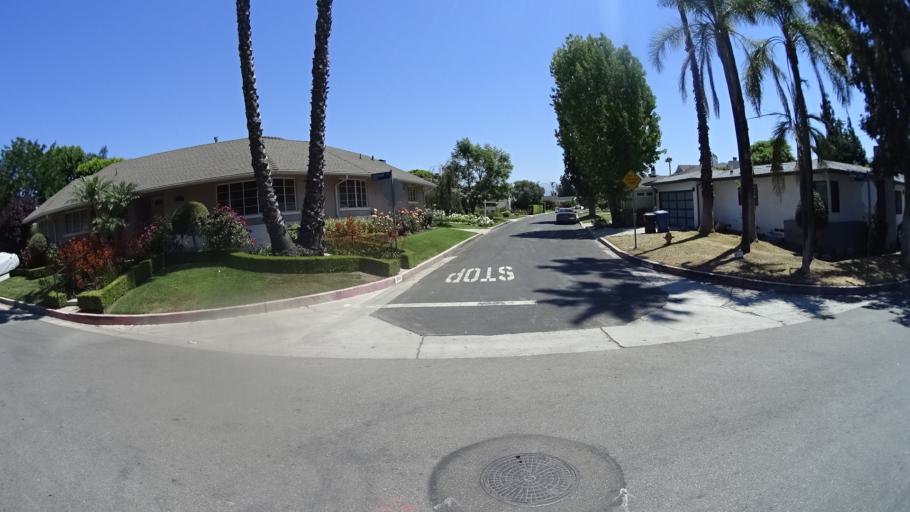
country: US
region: California
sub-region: Los Angeles County
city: Universal City
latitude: 34.1370
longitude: -118.3669
